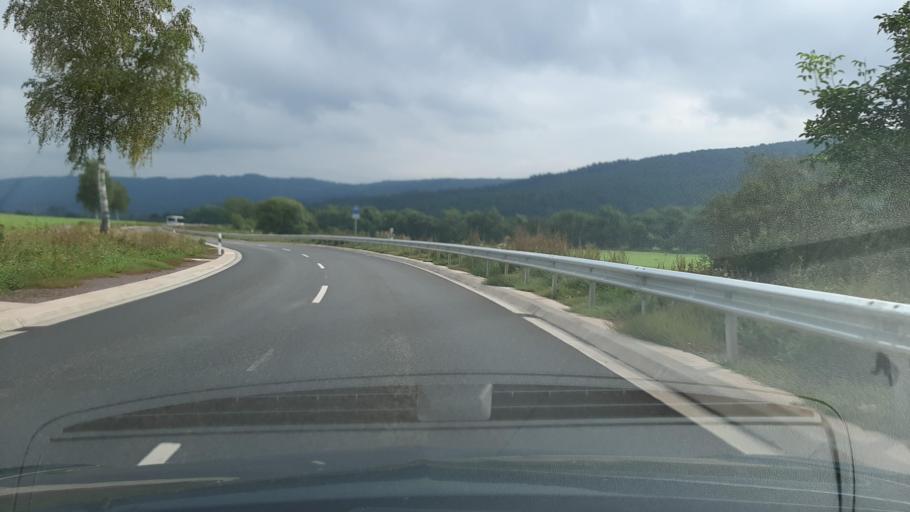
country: DE
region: Rheinland-Pfalz
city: Kinderbeuern
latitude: 50.0089
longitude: 7.0291
